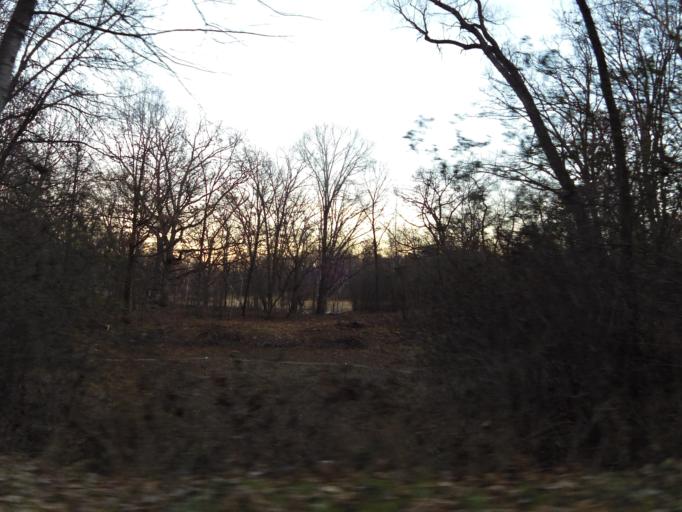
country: US
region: Minnesota
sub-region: Washington County
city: Grant
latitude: 45.0861
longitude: -92.8924
